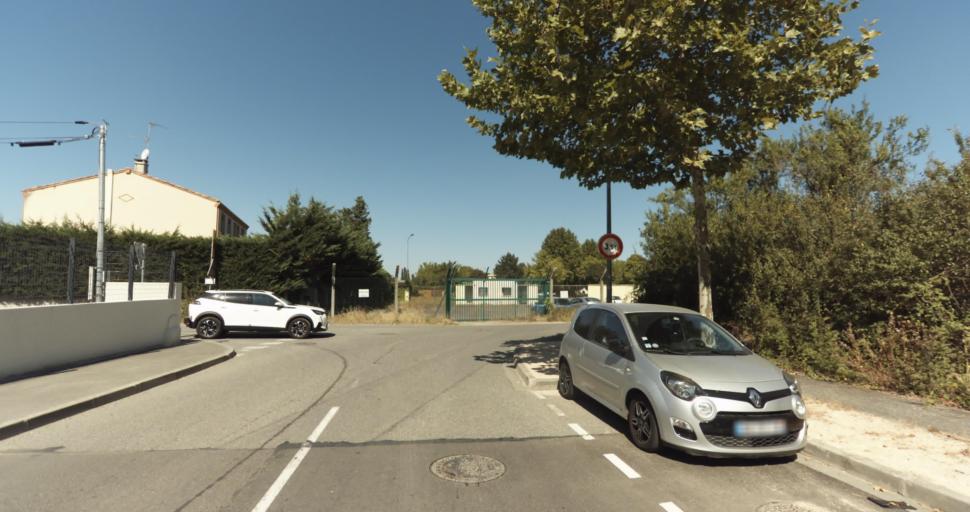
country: FR
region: Midi-Pyrenees
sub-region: Departement de la Haute-Garonne
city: L'Union
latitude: 43.6364
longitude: 1.4925
